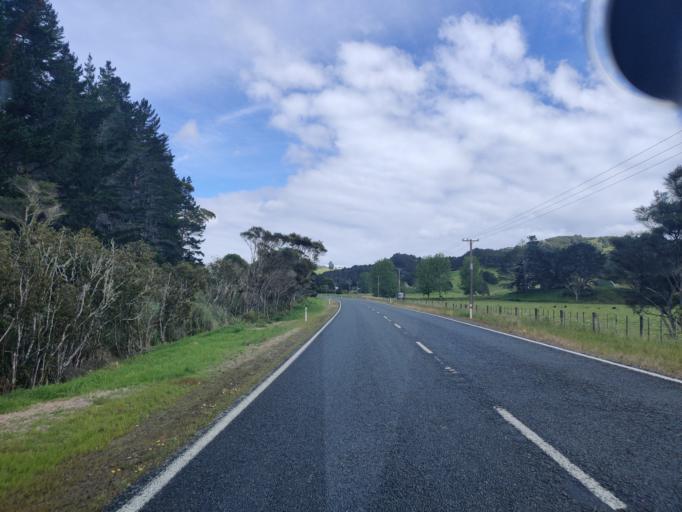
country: NZ
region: Northland
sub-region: Far North District
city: Taipa
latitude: -35.0556
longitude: 173.6882
